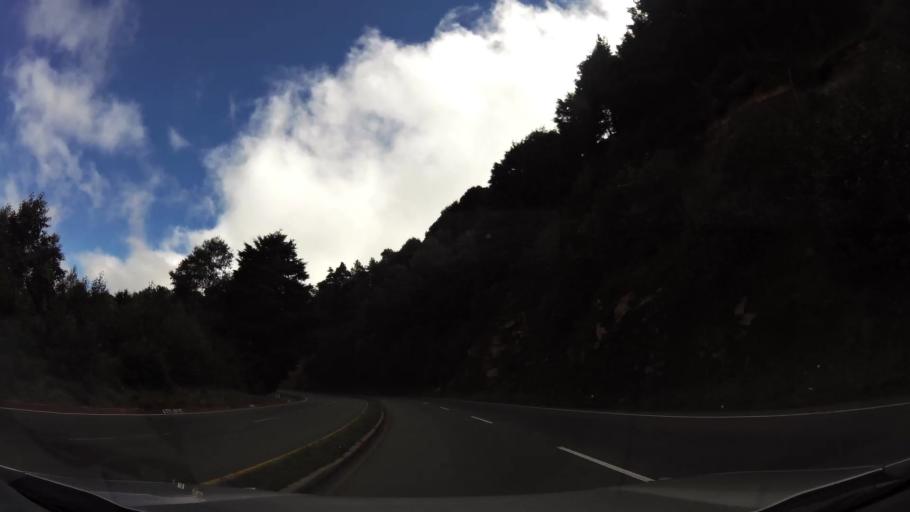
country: GT
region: Solola
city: Santa Catarina Ixtahuacan
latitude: 14.8385
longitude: -91.3919
